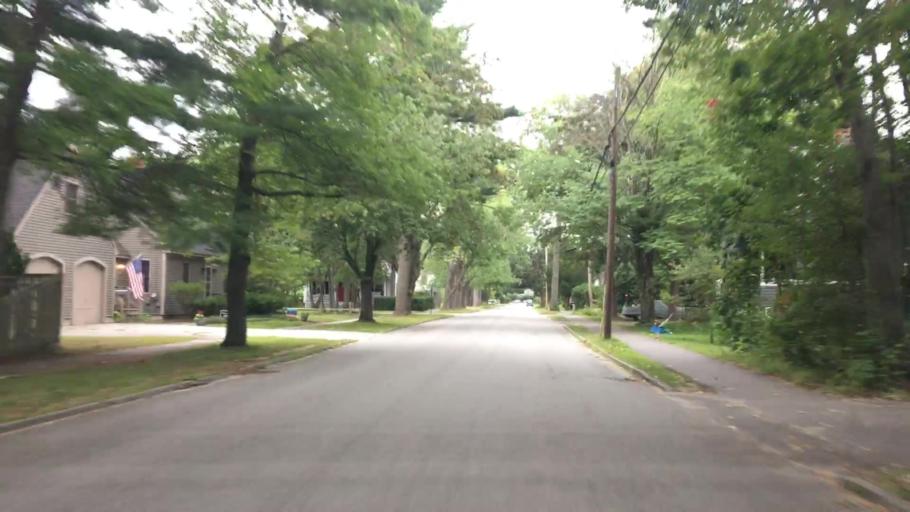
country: US
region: Maine
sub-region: Cumberland County
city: Brunswick
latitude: 43.9069
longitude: -69.9700
